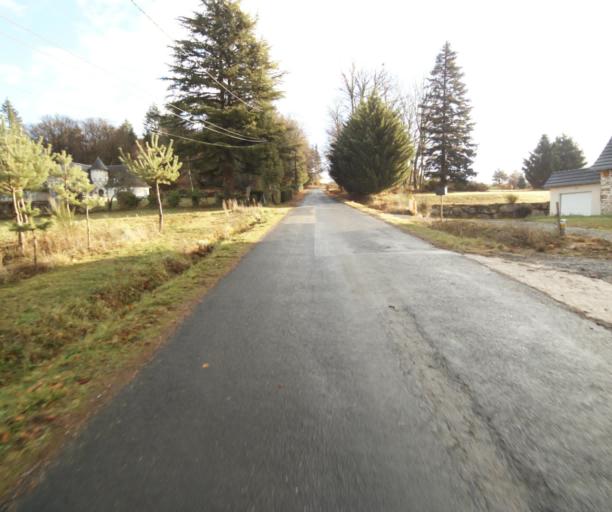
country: FR
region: Limousin
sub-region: Departement de la Correze
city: Saint-Mexant
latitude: 45.2705
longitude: 1.6365
